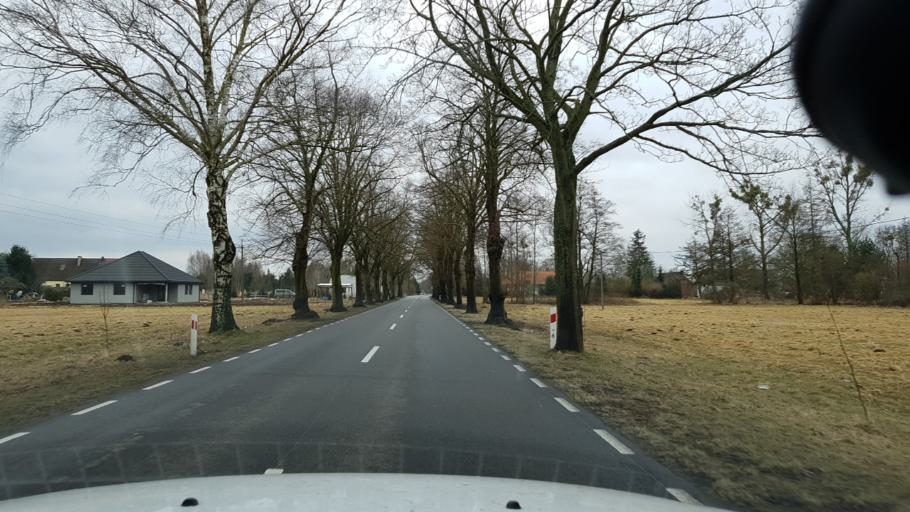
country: PL
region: West Pomeranian Voivodeship
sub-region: Powiat goleniowski
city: Goleniow
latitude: 53.6000
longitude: 14.7398
